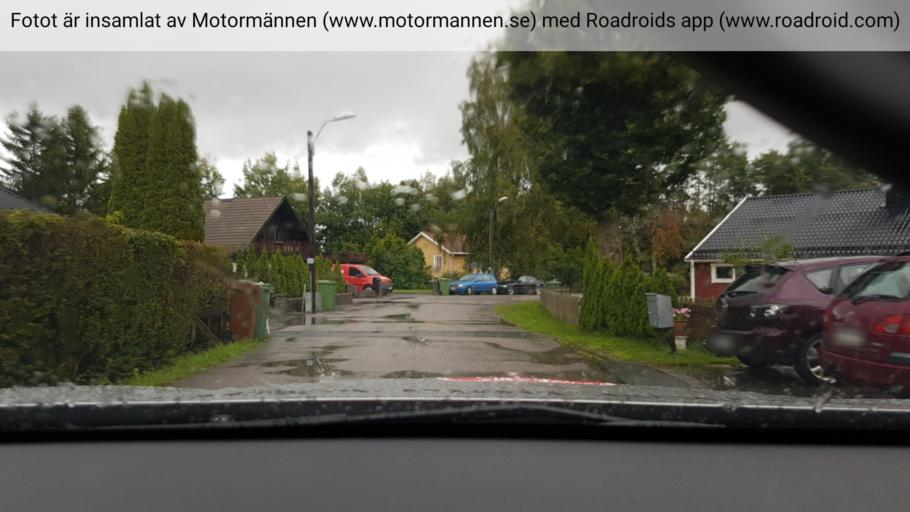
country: SE
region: Stockholm
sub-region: Haninge Kommun
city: Jordbro
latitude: 59.0956
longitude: 18.0406
